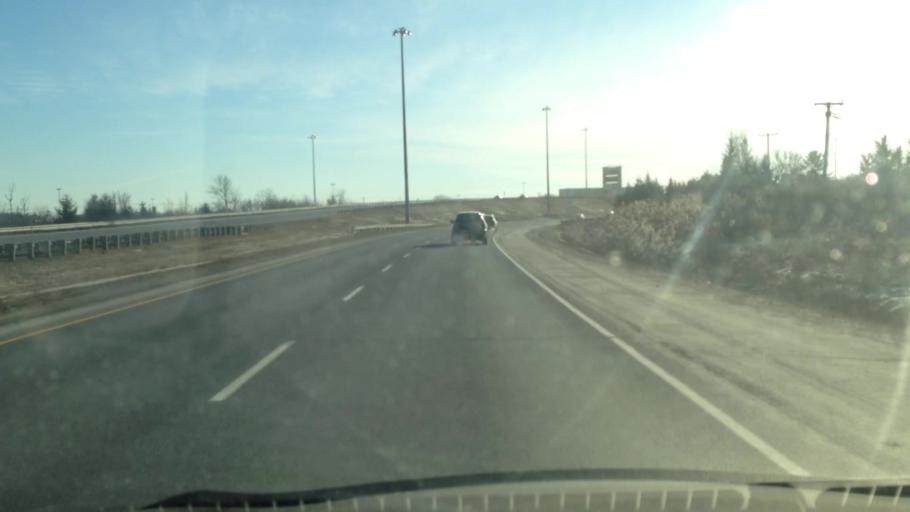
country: CA
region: Quebec
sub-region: Laurentides
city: Saint-Jerome
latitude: 45.7954
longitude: -74.0241
